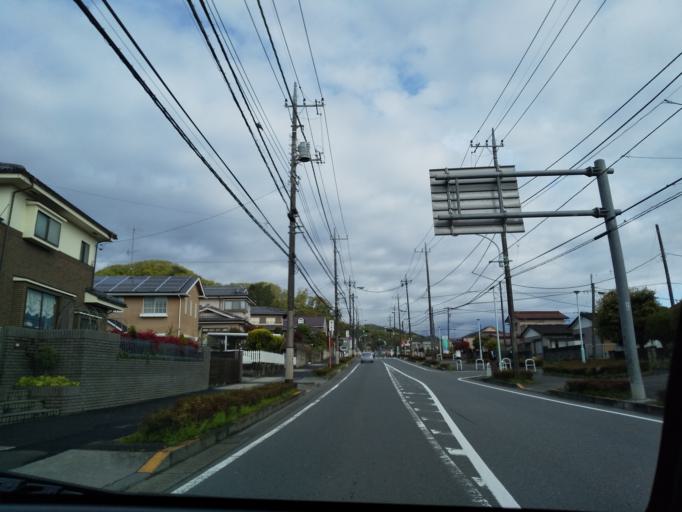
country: JP
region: Tokyo
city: Itsukaichi
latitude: 35.6730
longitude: 139.2591
